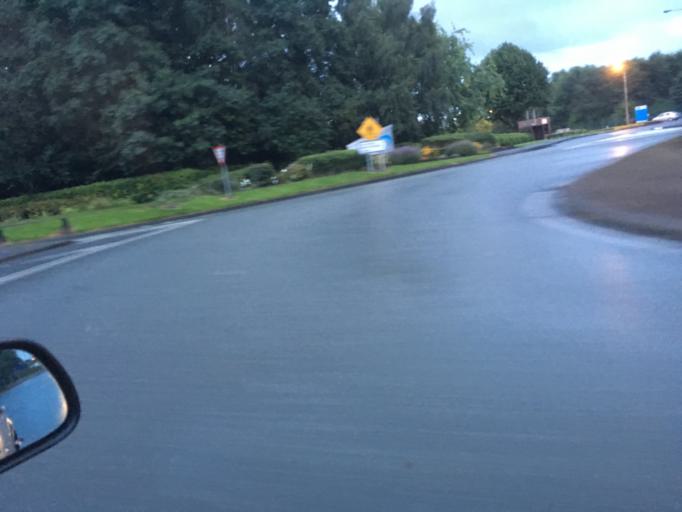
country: IE
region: Leinster
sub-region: Kildare
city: Droichead Nua
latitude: 53.1857
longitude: -6.7849
